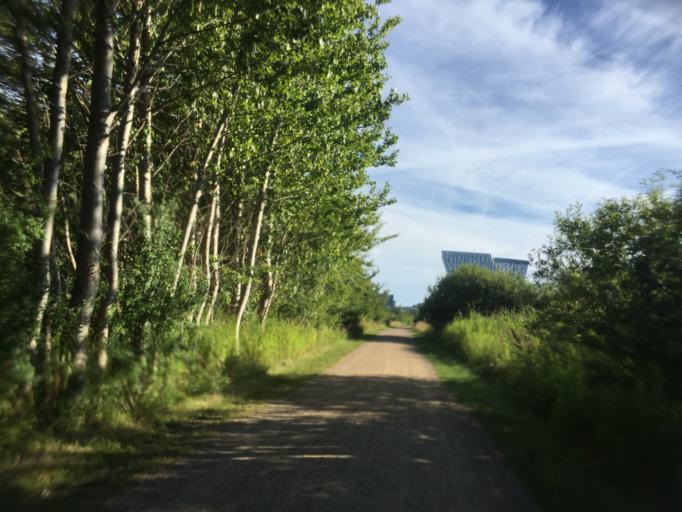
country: DK
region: Capital Region
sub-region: Tarnby Kommune
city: Tarnby
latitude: 55.6448
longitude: 12.5810
